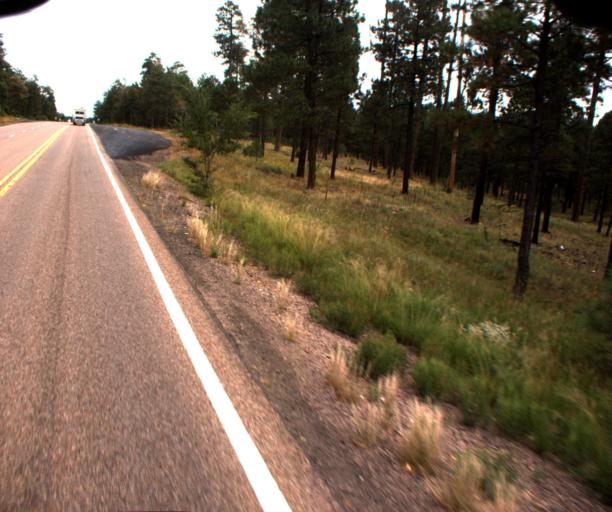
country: US
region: Arizona
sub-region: Navajo County
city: Heber-Overgaard
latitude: 34.3286
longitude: -110.8111
